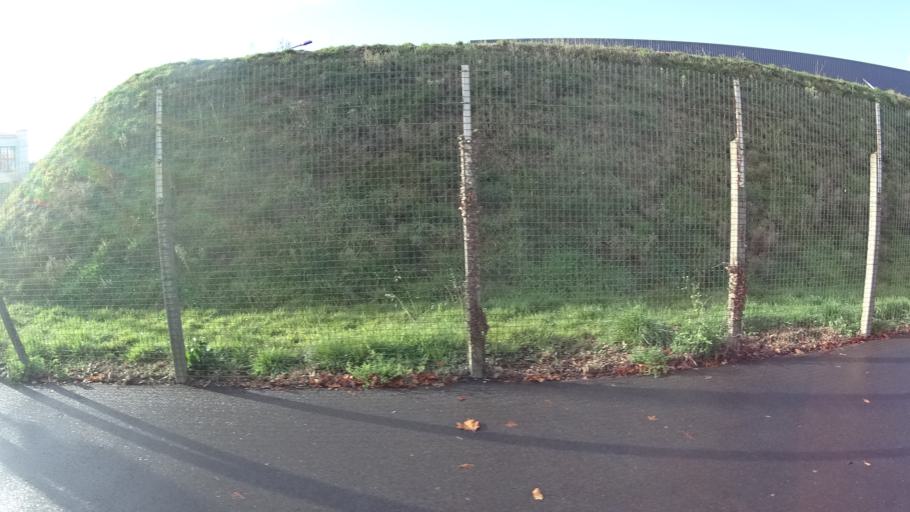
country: FR
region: Brittany
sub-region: Departement d'Ille-et-Vilaine
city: Redon
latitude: 47.6643
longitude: -2.0752
